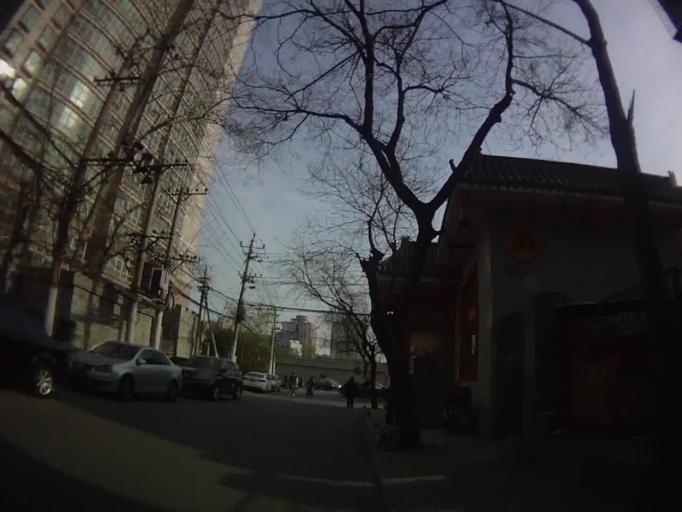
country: CN
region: Beijing
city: Chaowai
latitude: 39.9031
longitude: 116.4420
